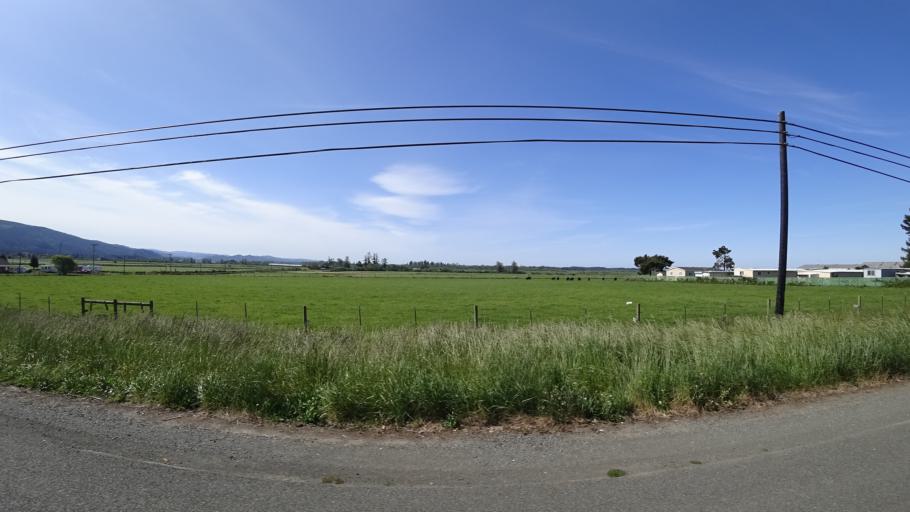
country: US
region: Oregon
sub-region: Curry County
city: Harbor
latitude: 41.9342
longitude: -124.1668
